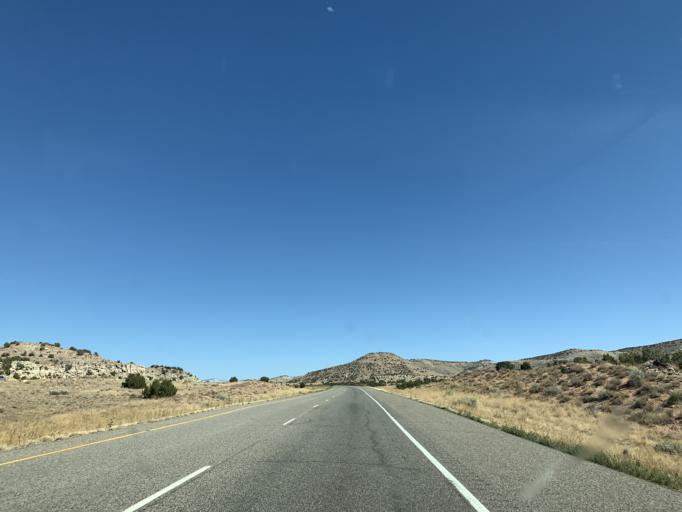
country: US
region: Colorado
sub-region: Mesa County
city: Loma
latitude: 39.2091
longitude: -108.9743
